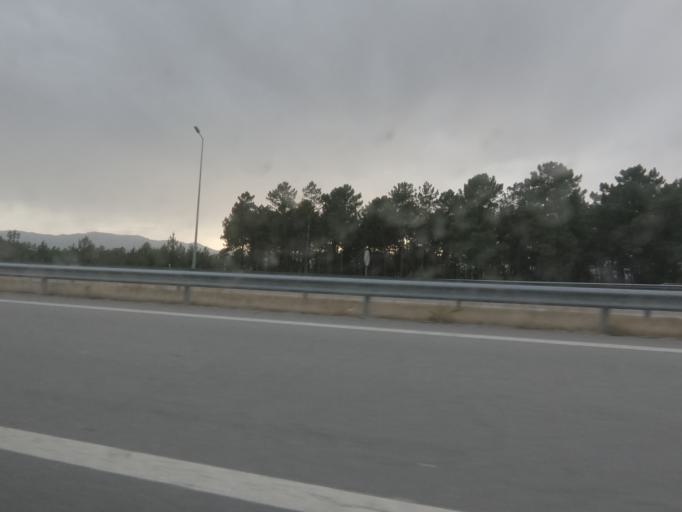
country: PT
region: Vila Real
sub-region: Vila Real
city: Vila Real
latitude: 41.2694
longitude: -7.6977
